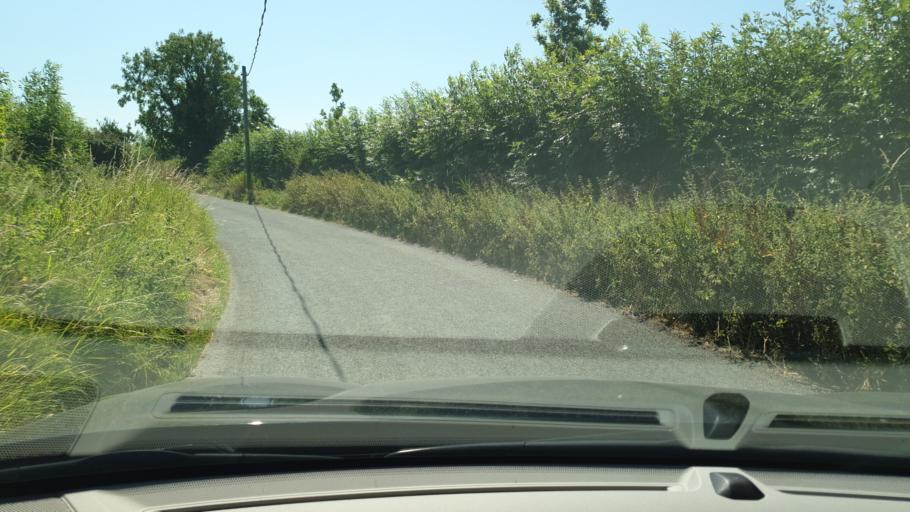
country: IE
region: Leinster
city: Hartstown
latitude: 53.4443
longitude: -6.4296
